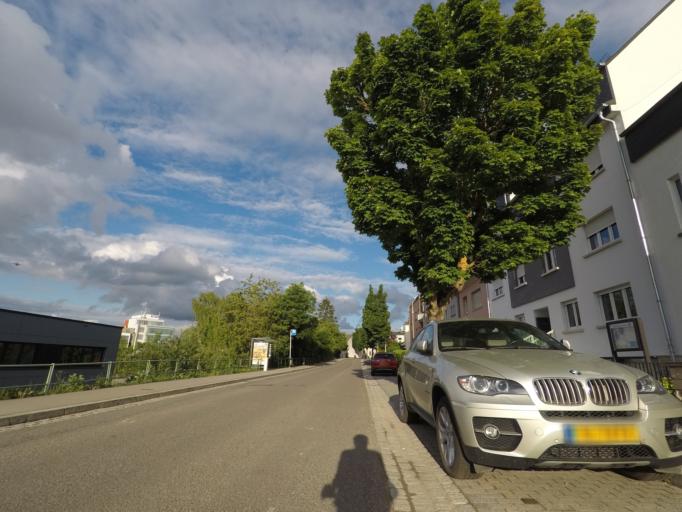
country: LU
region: Luxembourg
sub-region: Canton de Luxembourg
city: Luxembourg
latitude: 49.5939
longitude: 6.1274
